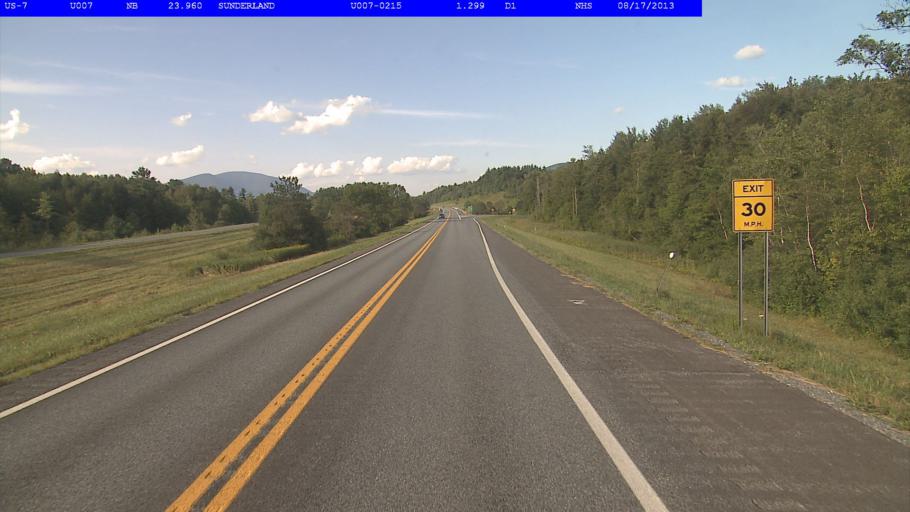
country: US
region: Vermont
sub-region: Bennington County
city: Arlington
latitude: 43.0433
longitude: -73.1315
